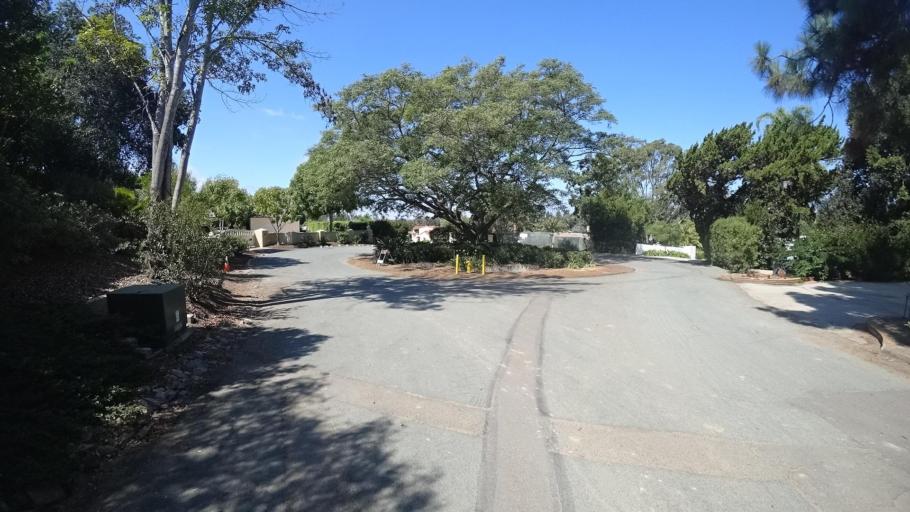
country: US
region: California
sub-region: San Diego County
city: Rancho Santa Fe
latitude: 33.0249
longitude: -117.1981
